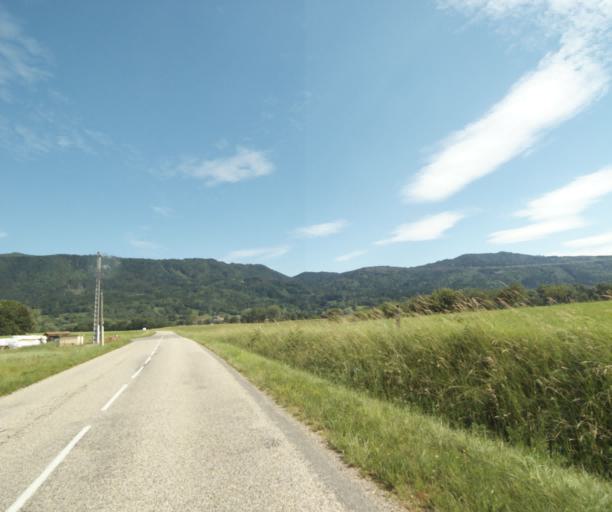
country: FR
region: Rhone-Alpes
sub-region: Departement de la Haute-Savoie
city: Perrignier
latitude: 46.2939
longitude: 6.4322
